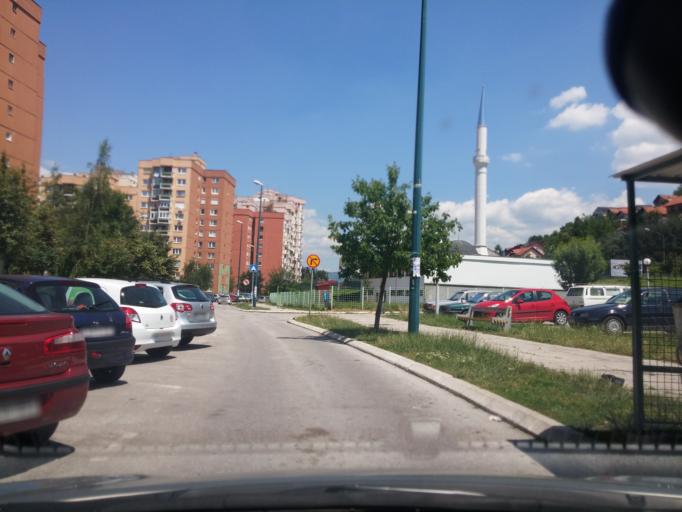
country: BA
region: Federation of Bosnia and Herzegovina
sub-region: Kanton Sarajevo
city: Sarajevo
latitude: 43.8411
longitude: 18.3506
